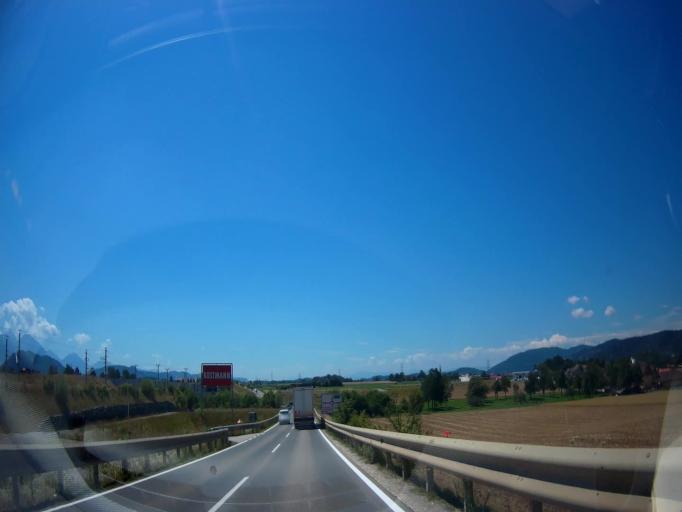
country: AT
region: Carinthia
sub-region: Politischer Bezirk Volkermarkt
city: Voelkermarkt
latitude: 46.6273
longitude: 14.6387
